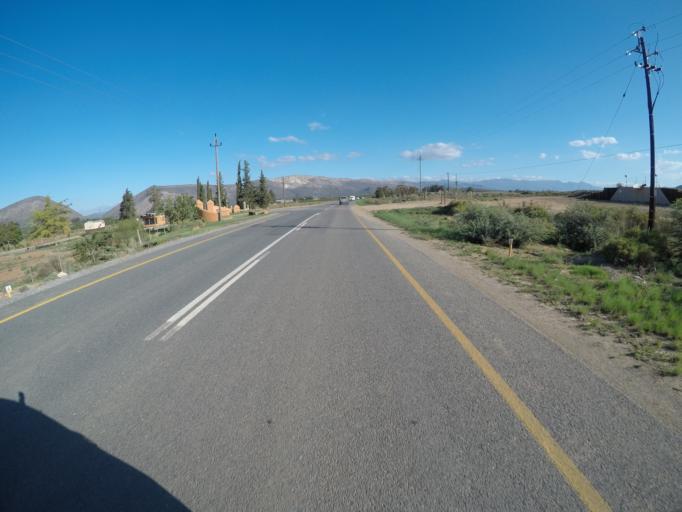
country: ZA
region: Western Cape
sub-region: Cape Winelands District Municipality
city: Ashton
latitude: -33.8059
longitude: 19.7822
